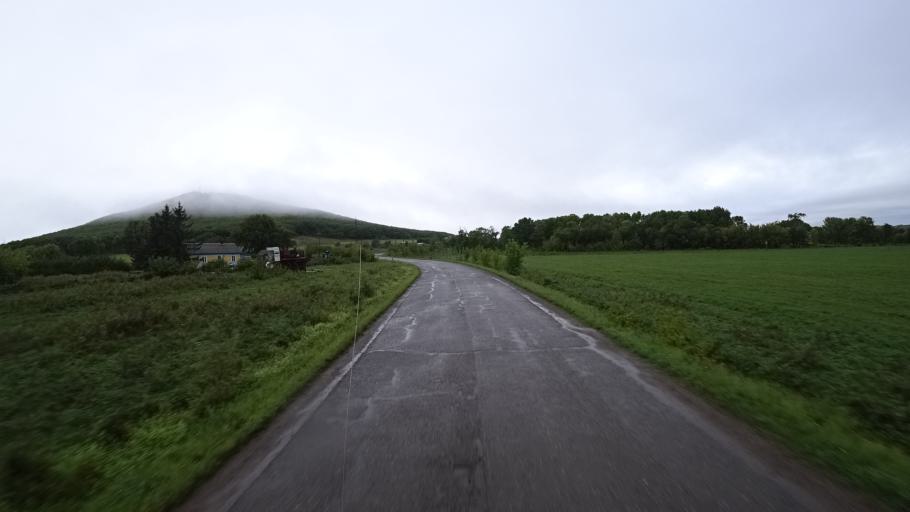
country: RU
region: Primorskiy
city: Monastyrishche
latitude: 44.2585
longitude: 132.4195
